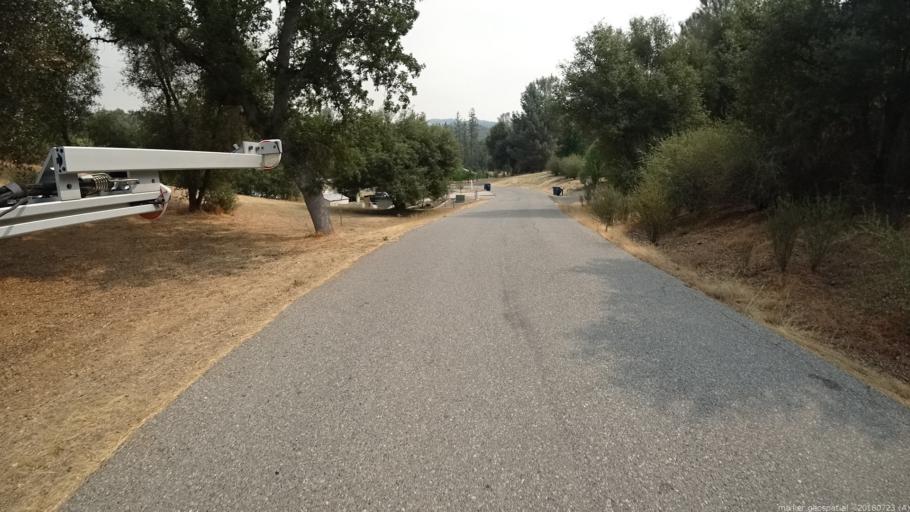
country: US
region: California
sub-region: Madera County
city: Oakhurst
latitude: 37.3541
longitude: -119.6790
